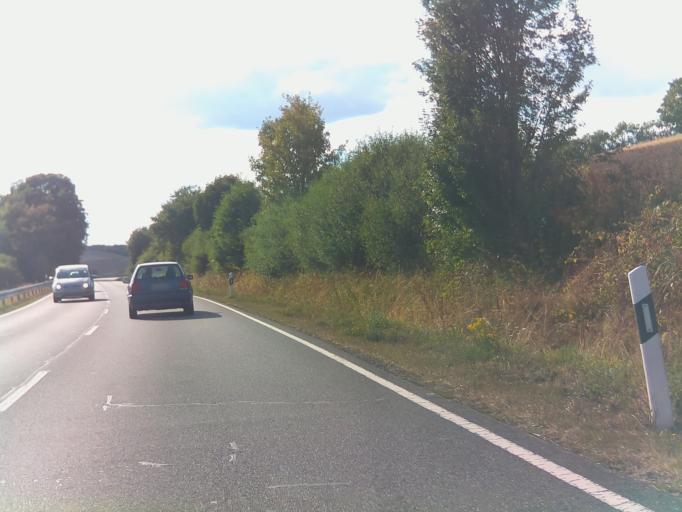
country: DE
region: Hesse
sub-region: Regierungsbezirk Kassel
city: Dipperz
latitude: 50.5277
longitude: 9.8370
